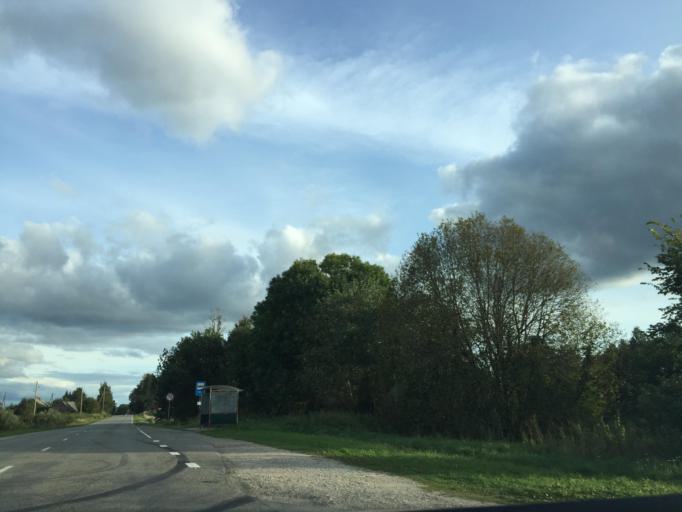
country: LV
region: Nereta
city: Nereta
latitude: 56.2722
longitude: 25.1705
